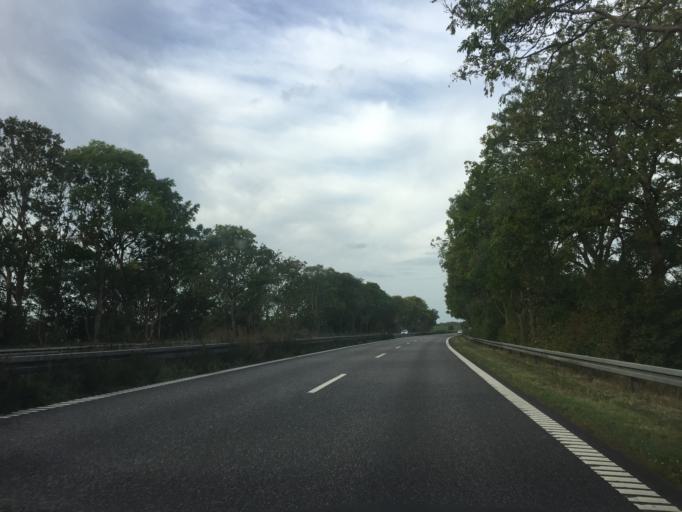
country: DK
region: Zealand
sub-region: Guldborgsund Kommune
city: Sakskobing
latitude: 54.7876
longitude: 11.5819
